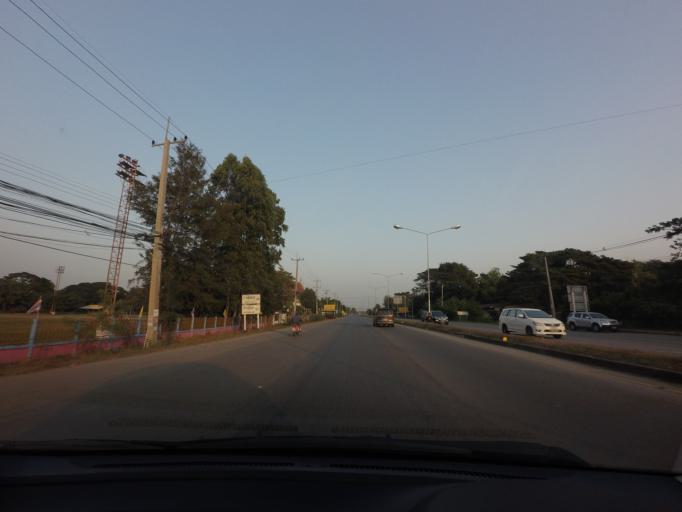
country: TH
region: Sukhothai
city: Sukhothai
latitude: 17.0263
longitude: 99.8832
